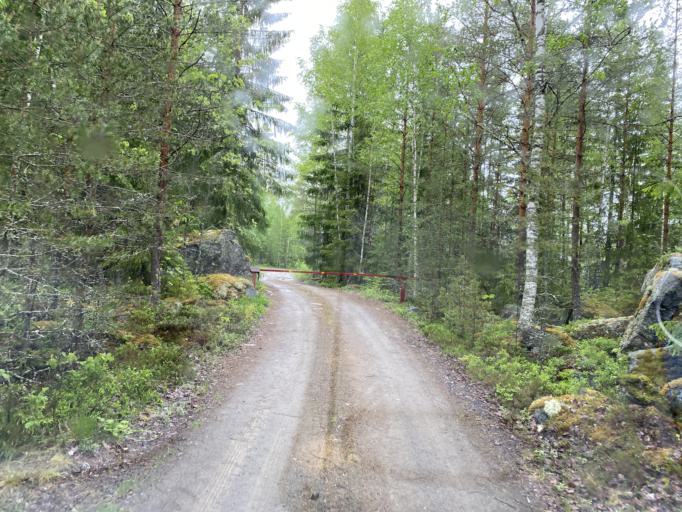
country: FI
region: Pirkanmaa
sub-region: Etelae-Pirkanmaa
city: Urjala
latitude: 60.9568
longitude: 23.5565
